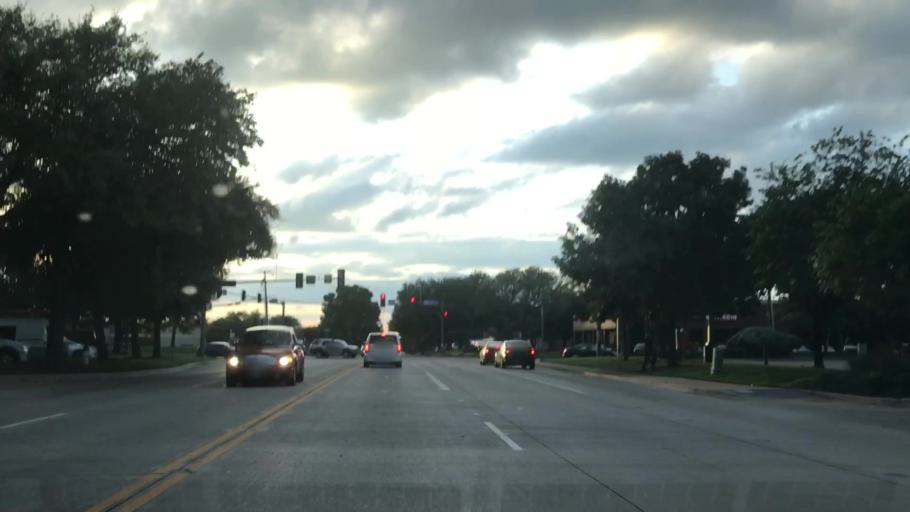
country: US
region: Texas
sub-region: Dallas County
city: Addison
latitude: 32.9563
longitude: -96.8537
